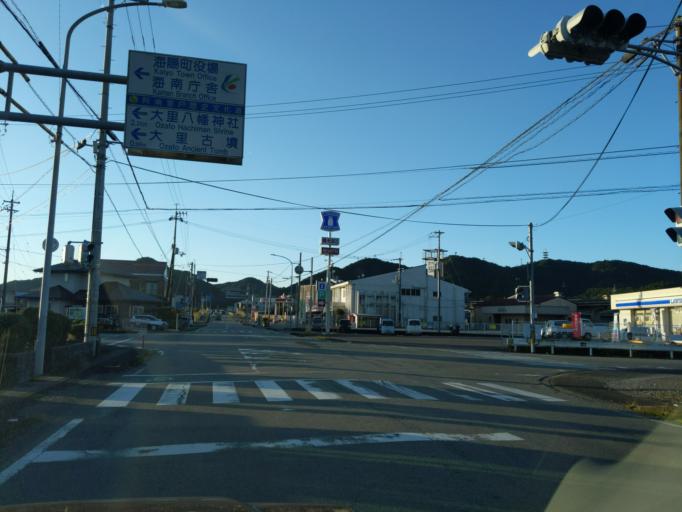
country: JP
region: Kochi
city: Muroto-misakicho
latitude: 33.6020
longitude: 134.3515
